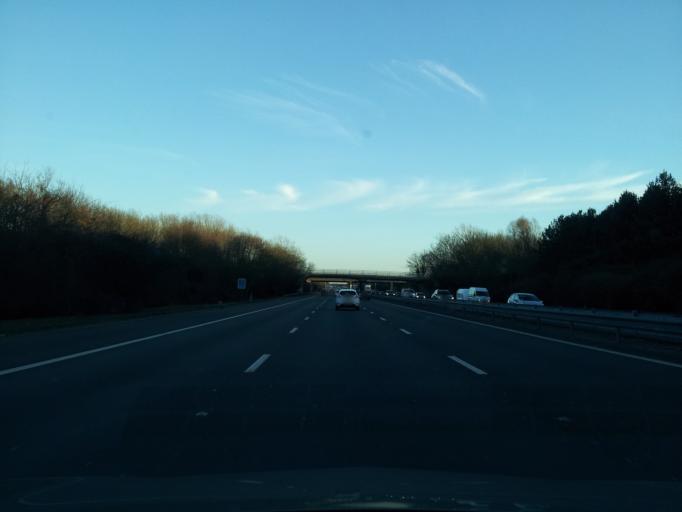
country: GB
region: England
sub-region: Milton Keynes
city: Newport Pagnell
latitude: 52.0745
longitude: -0.7328
